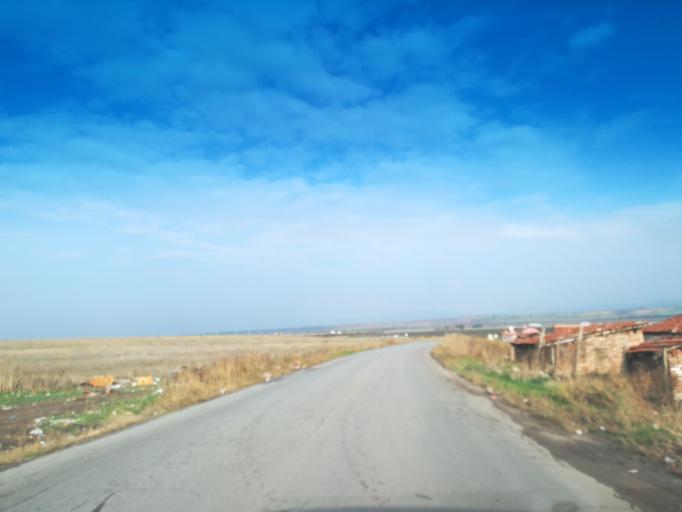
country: BG
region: Stara Zagora
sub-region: Obshtina Chirpan
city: Chirpan
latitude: 42.2021
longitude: 25.3092
